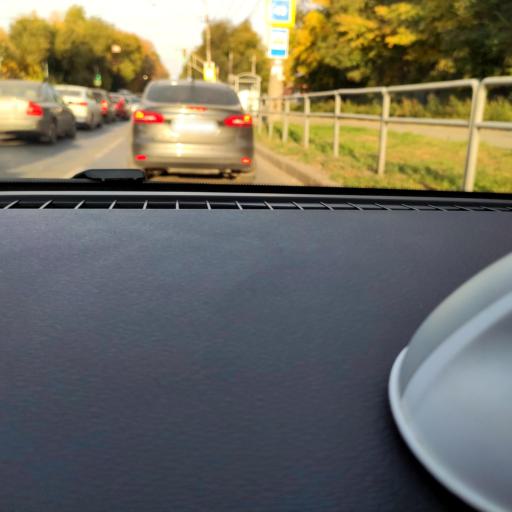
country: RU
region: Samara
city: Samara
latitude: 53.2227
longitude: 50.2342
